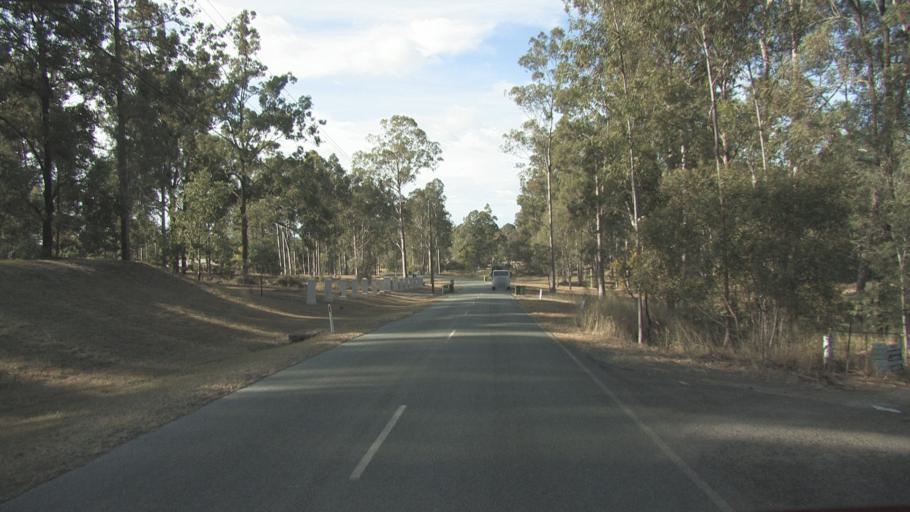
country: AU
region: Queensland
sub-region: Logan
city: Cedar Vale
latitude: -27.8803
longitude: 152.9994
